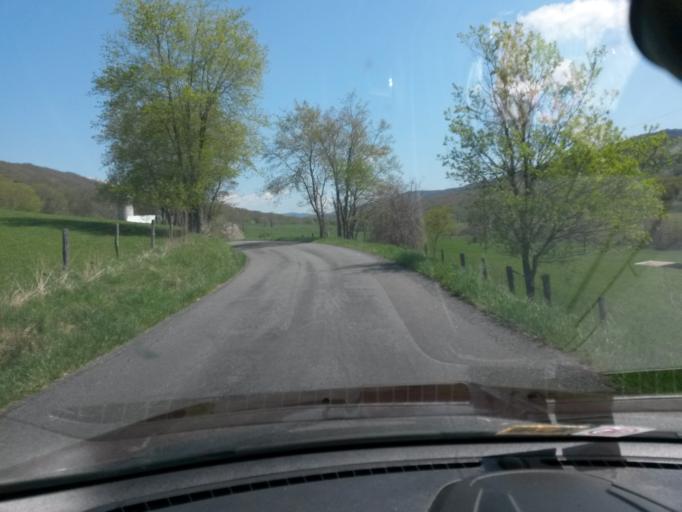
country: US
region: Virginia
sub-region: Highland County
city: Monterey
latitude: 38.2414
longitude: -79.6512
